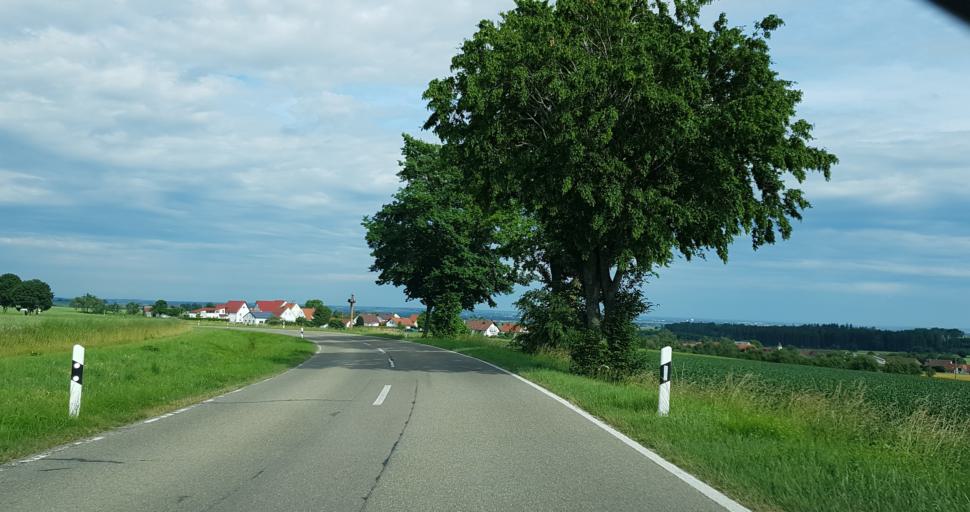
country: DE
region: Baden-Wuerttemberg
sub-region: Tuebingen Region
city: Altheim
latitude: 48.3129
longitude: 9.7799
